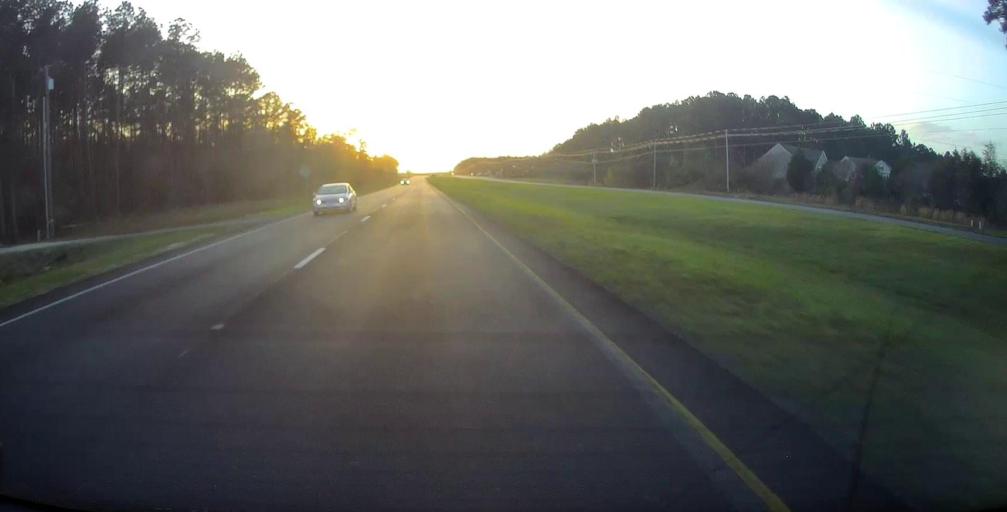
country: US
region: Georgia
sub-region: Chatham County
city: Pooler
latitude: 32.1624
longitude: -81.2509
